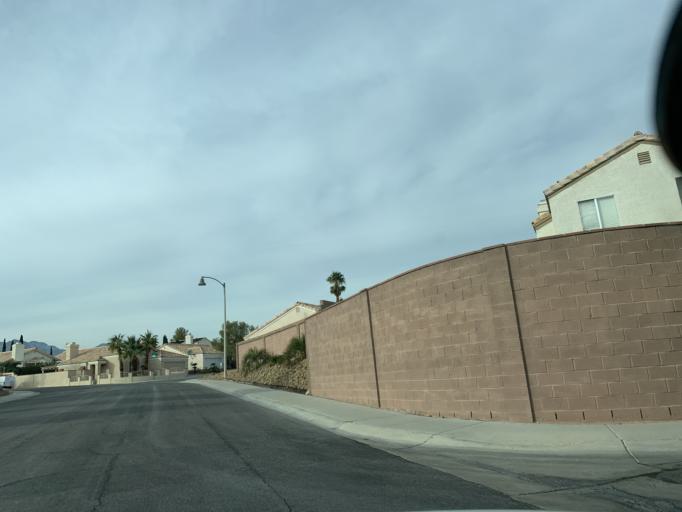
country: US
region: Nevada
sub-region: Clark County
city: Summerlin South
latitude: 36.1414
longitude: -115.3027
